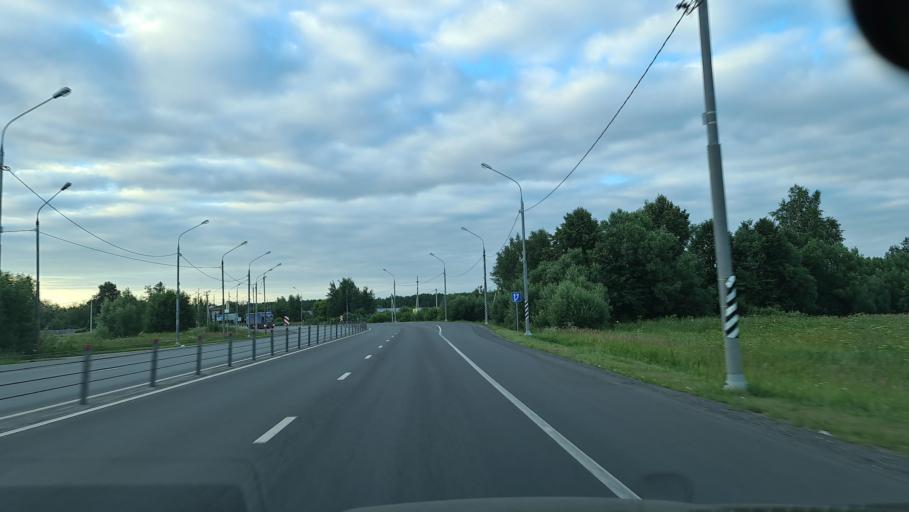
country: RU
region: Moskovskaya
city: Malaya Dubna
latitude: 55.8729
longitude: 38.9632
